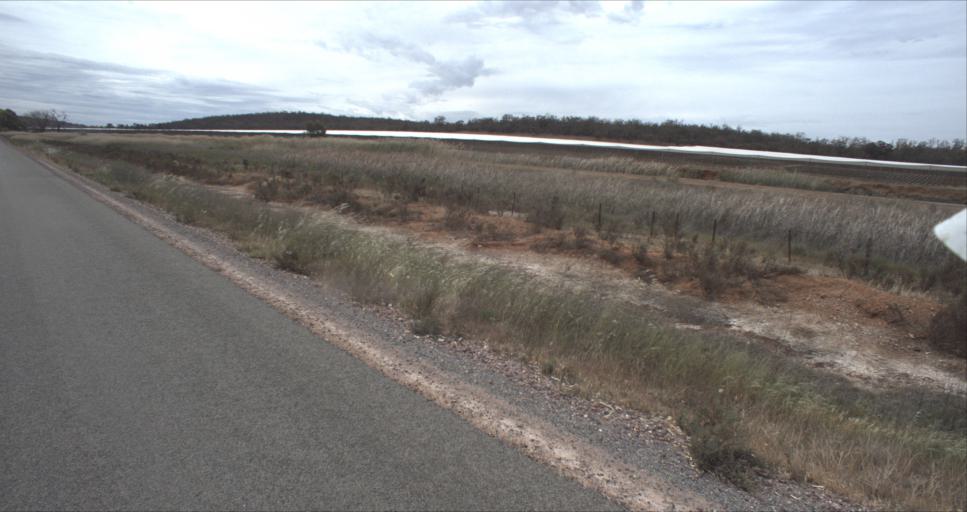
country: AU
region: New South Wales
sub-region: Leeton
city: Leeton
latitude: -34.4335
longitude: 146.3767
